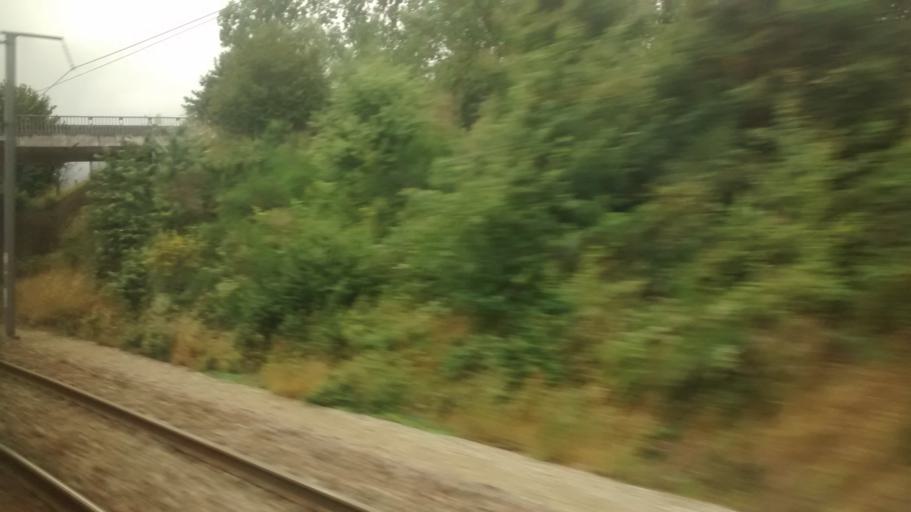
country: FR
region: Pays de la Loire
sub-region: Departement de la Sarthe
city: Thorigne-sur-Due
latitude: 48.0464
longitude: 0.5501
